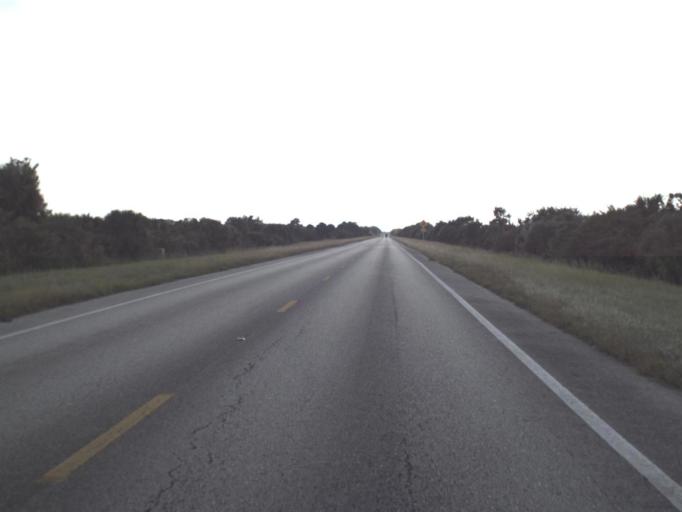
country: US
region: Florida
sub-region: Brevard County
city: Port Saint John
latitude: 28.4793
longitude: -80.8539
